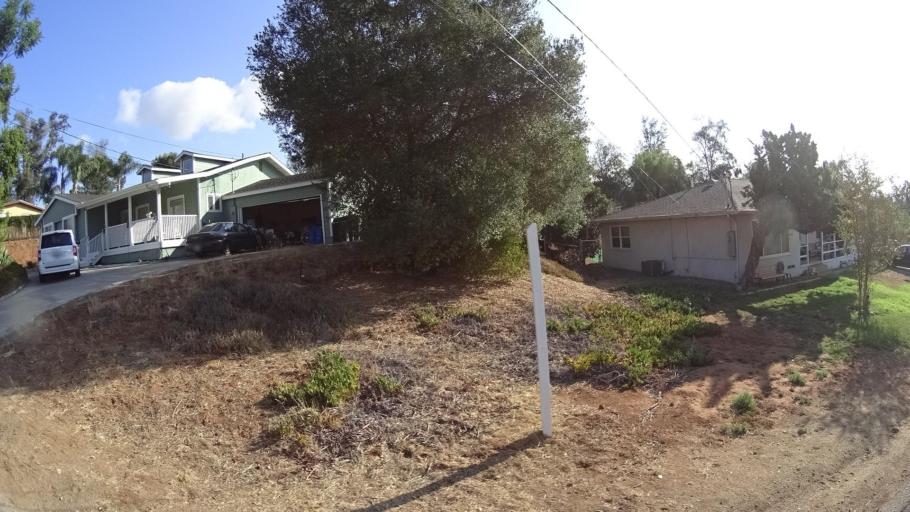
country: US
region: California
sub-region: San Diego County
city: Eucalyptus Hills
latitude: 32.8859
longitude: -116.9448
